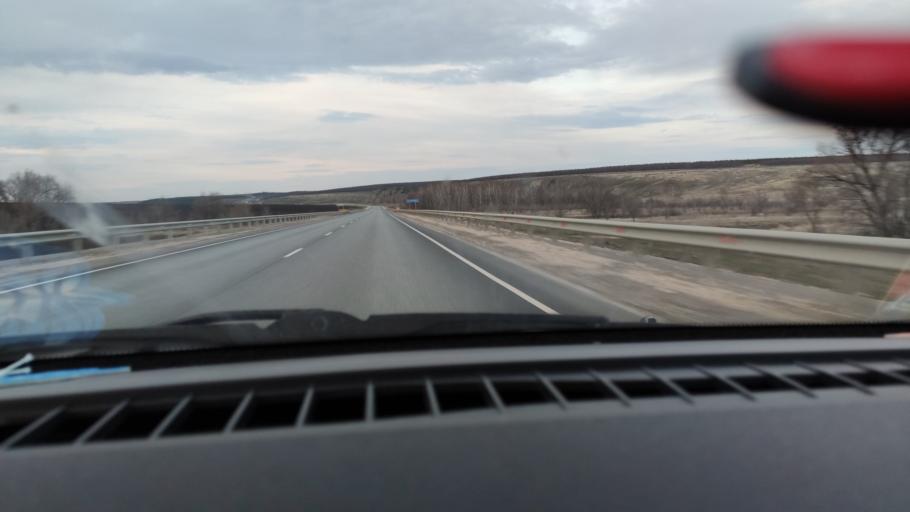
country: RU
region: Saratov
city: Yelshanka
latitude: 51.8557
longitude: 46.4943
